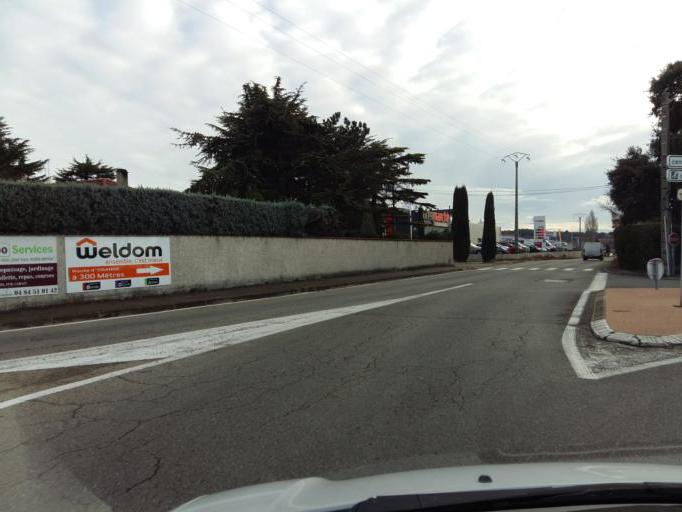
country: FR
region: Provence-Alpes-Cote d'Azur
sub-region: Departement du Vaucluse
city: Valreas
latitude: 44.3734
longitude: 4.9803
